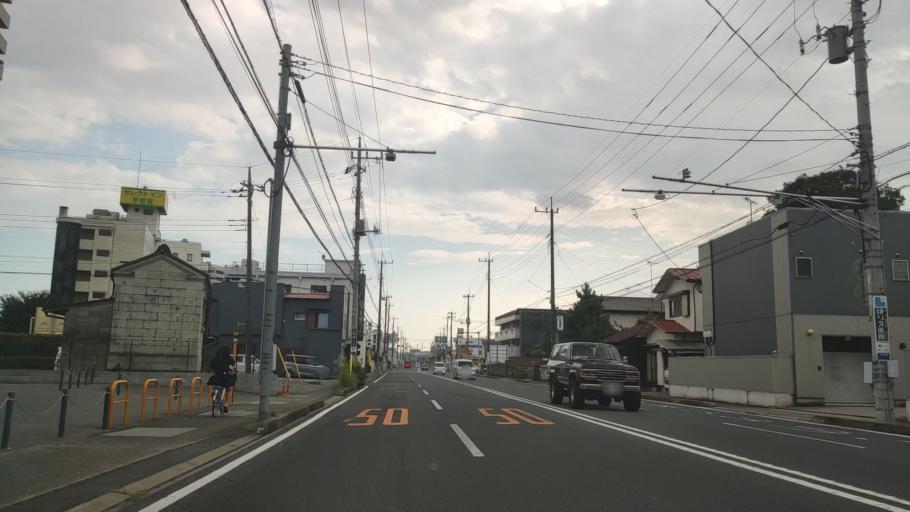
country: JP
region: Tochigi
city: Utsunomiya-shi
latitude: 36.5727
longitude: 139.9037
